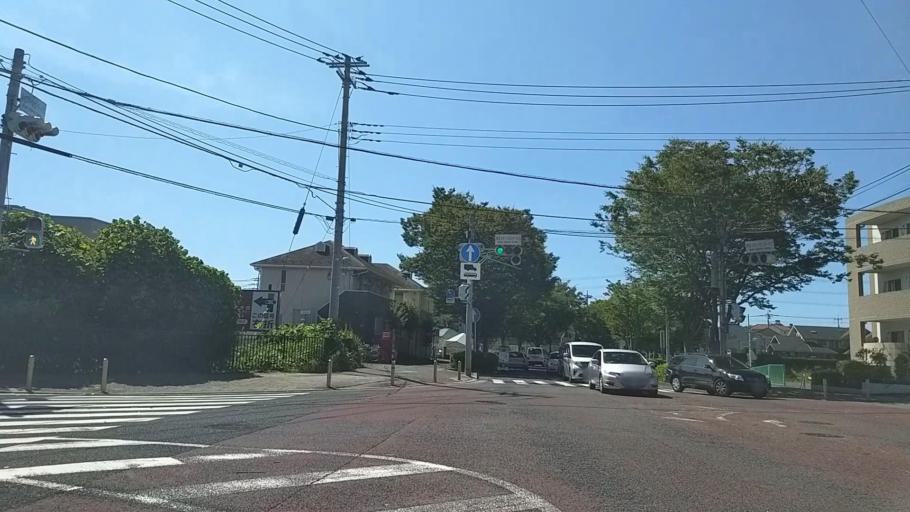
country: JP
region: Tokyo
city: Chofugaoka
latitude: 35.5994
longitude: 139.5077
